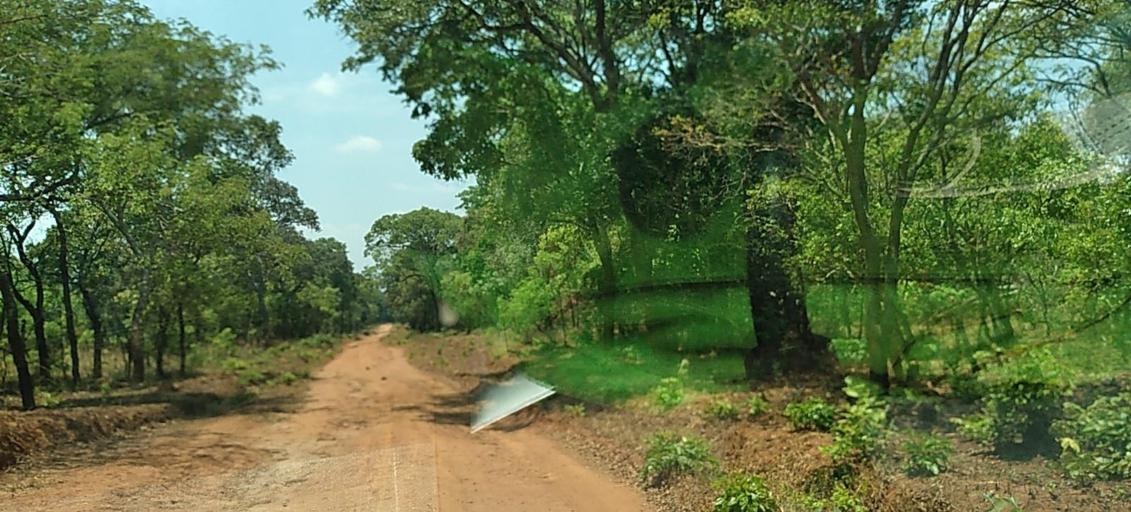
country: CD
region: Katanga
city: Kolwezi
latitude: -11.3541
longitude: 25.2113
